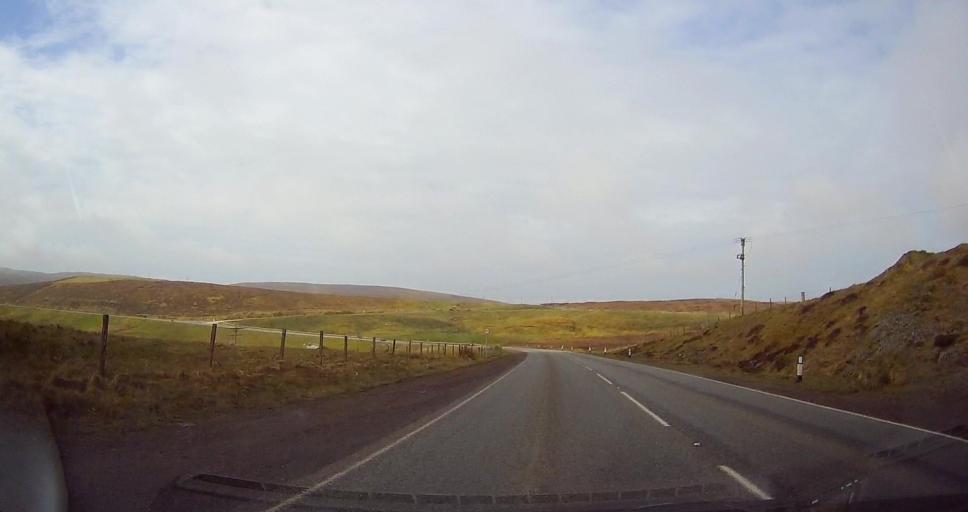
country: GB
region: Scotland
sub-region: Shetland Islands
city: Lerwick
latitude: 60.1392
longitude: -1.2050
